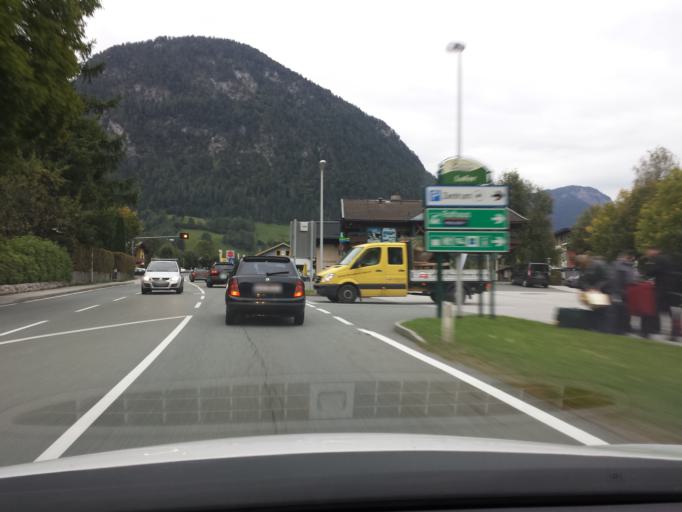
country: AT
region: Salzburg
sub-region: Politischer Bezirk Zell am See
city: Lofer
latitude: 47.5871
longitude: 12.6954
